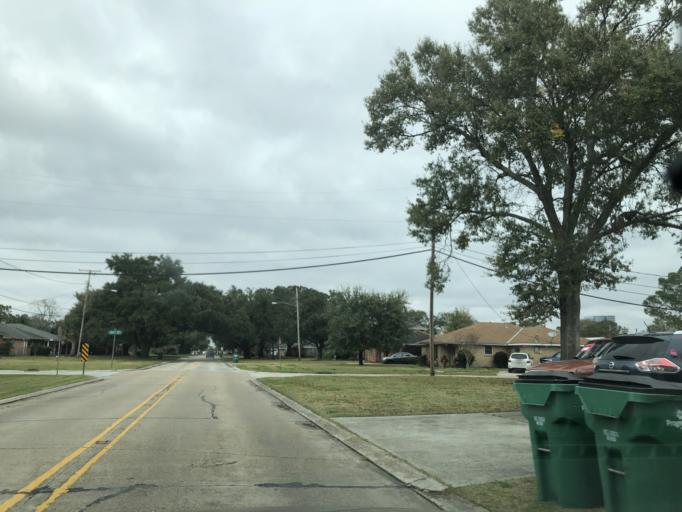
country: US
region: Louisiana
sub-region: Jefferson Parish
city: Metairie
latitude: 29.9865
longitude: -90.1601
